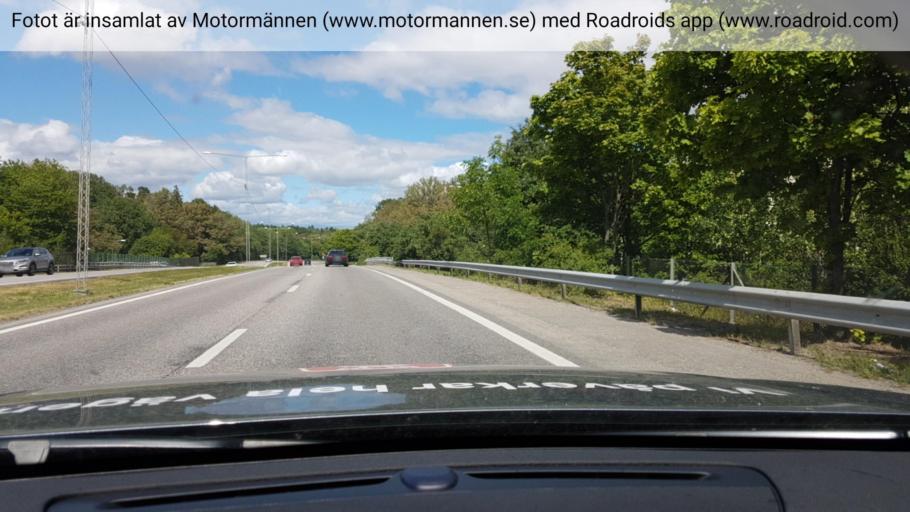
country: SE
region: Stockholm
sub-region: Huddinge Kommun
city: Huddinge
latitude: 59.2640
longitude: 18.0061
